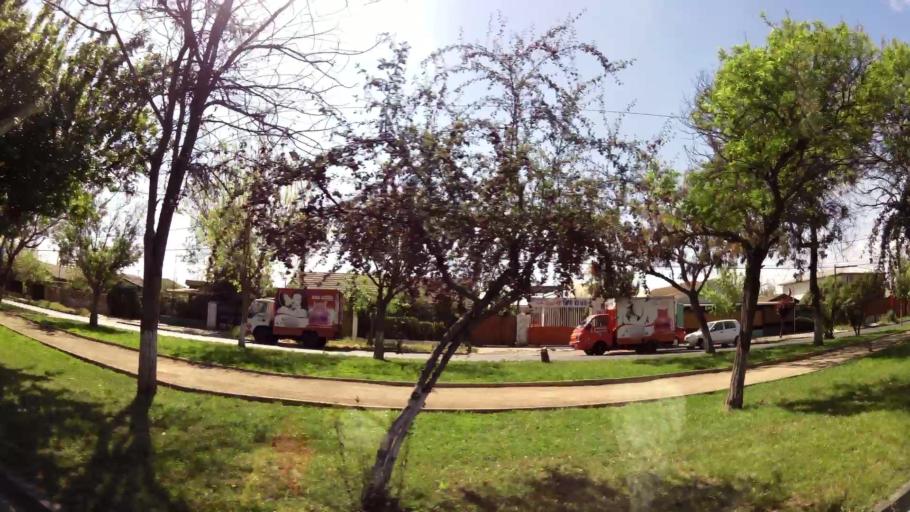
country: CL
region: Santiago Metropolitan
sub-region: Provincia de Santiago
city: La Pintana
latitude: -33.5272
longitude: -70.6431
